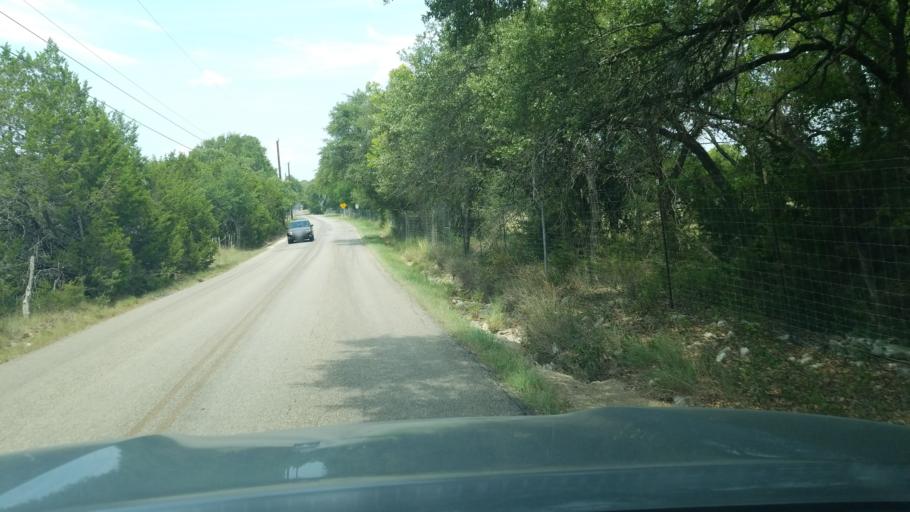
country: US
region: Texas
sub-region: Comal County
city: Bulverde
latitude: 29.7598
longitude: -98.4641
